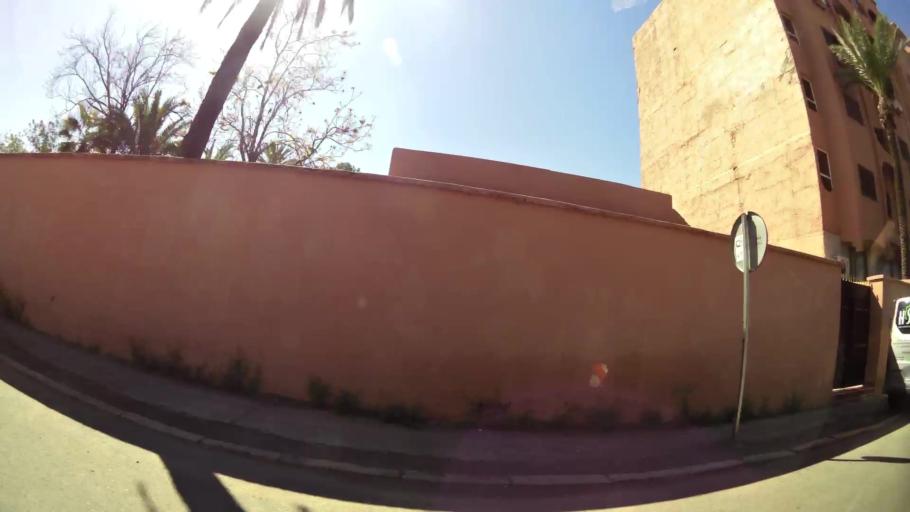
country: MA
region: Marrakech-Tensift-Al Haouz
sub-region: Marrakech
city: Marrakesh
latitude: 31.6372
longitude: -8.0056
